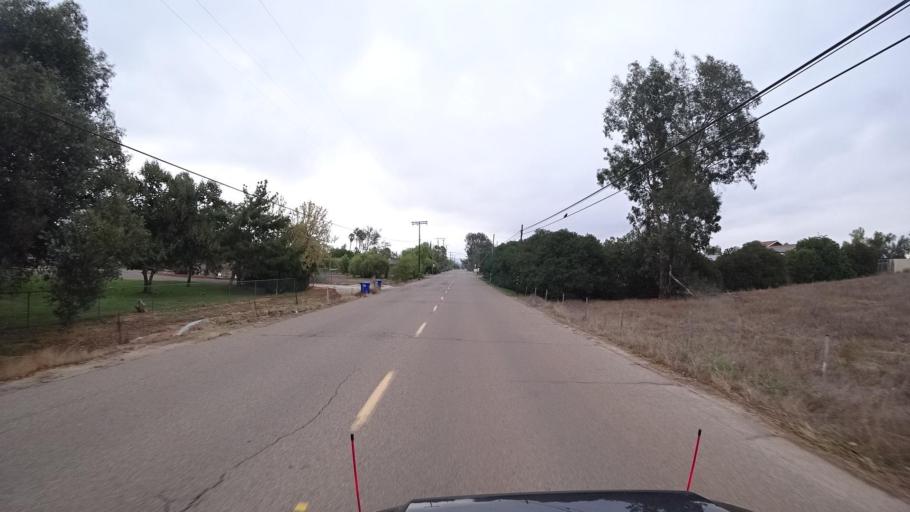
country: US
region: California
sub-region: San Diego County
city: Ramona
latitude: 33.0404
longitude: -116.8944
